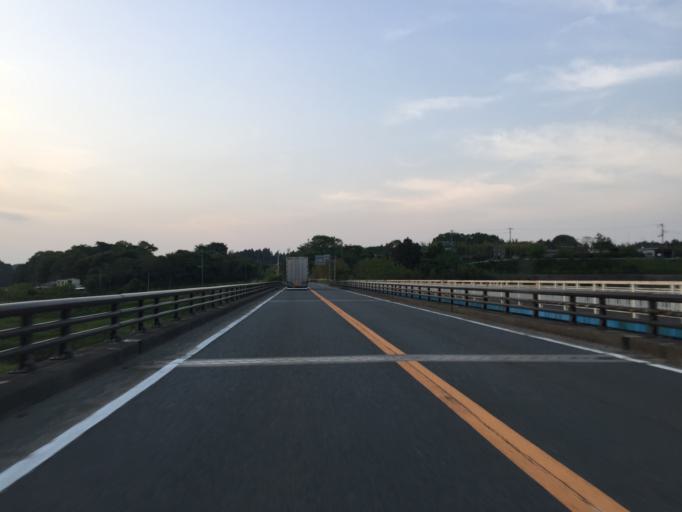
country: JP
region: Fukushima
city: Namie
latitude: 37.4968
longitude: 141.0014
